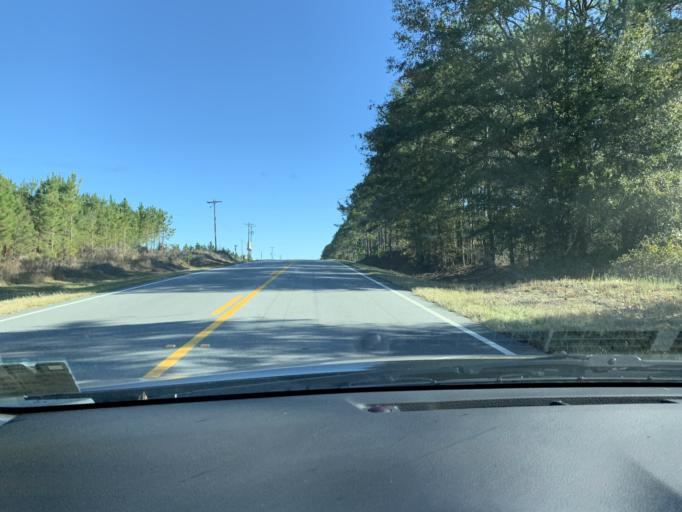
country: US
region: Georgia
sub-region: Ben Hill County
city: Fitzgerald
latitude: 31.7591
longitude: -83.1209
